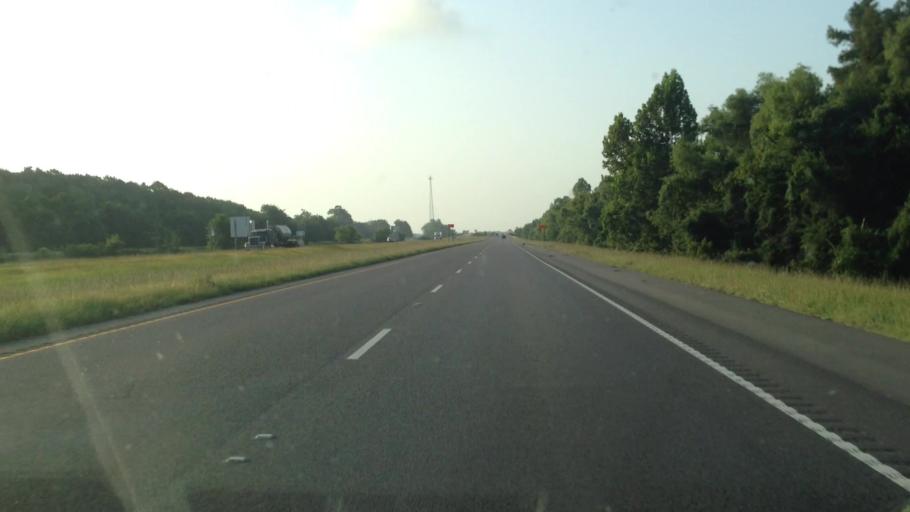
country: US
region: Louisiana
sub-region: Rapides Parish
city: Boyce
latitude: 31.3988
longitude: -92.7020
